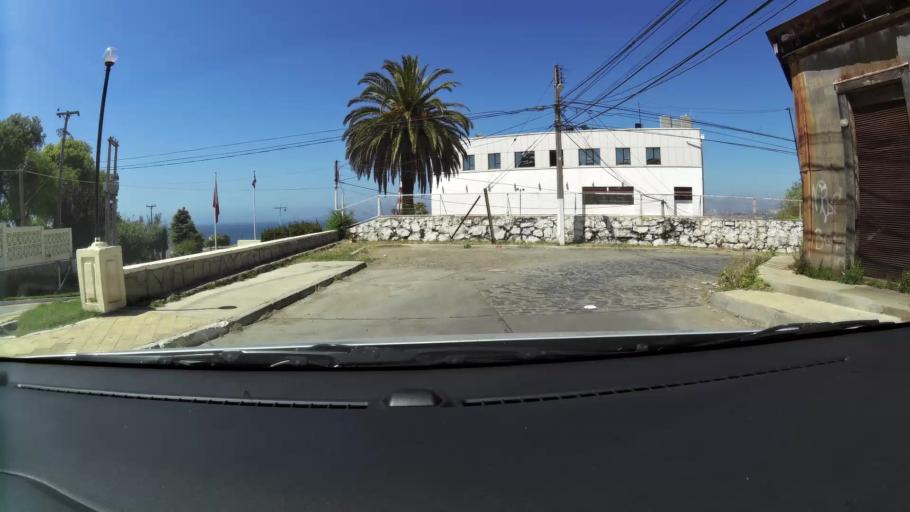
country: CL
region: Valparaiso
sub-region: Provincia de Valparaiso
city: Valparaiso
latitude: -33.0297
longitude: -71.6304
